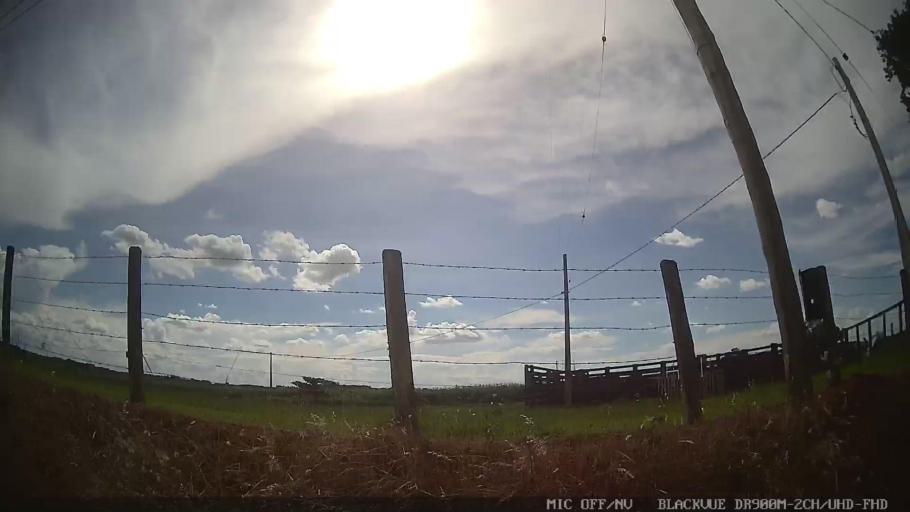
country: BR
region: Sao Paulo
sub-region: Conchas
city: Conchas
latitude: -23.0357
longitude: -47.9956
